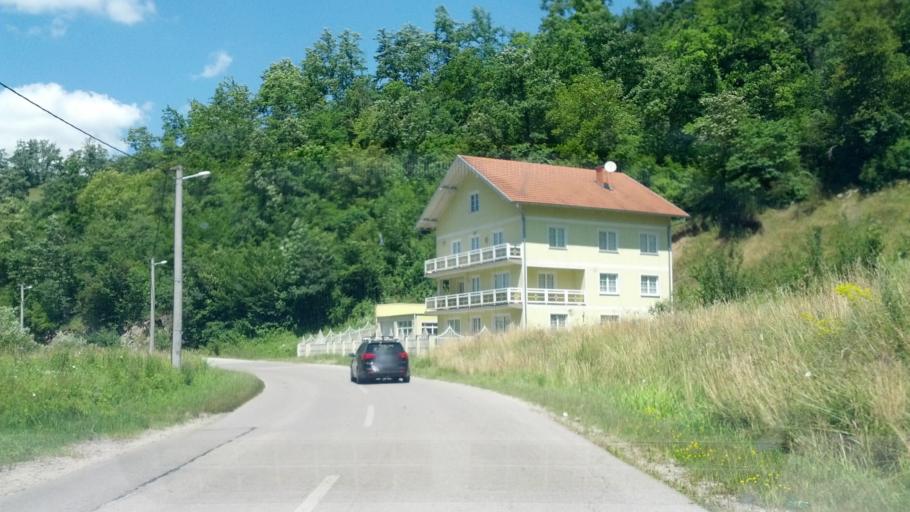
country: BA
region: Federation of Bosnia and Herzegovina
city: Jezerski
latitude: 45.0210
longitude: 16.0879
